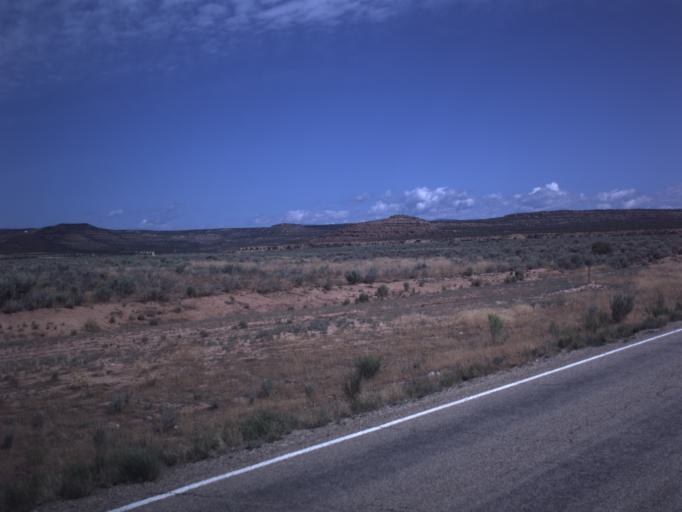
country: US
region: Utah
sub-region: Duchesne County
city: Duchesne
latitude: 40.2591
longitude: -110.3840
